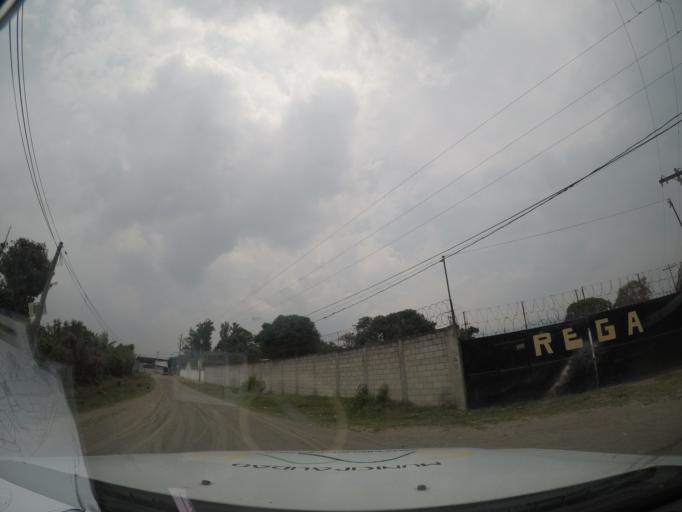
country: GT
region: Guatemala
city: Petapa
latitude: 14.5076
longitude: -90.5513
